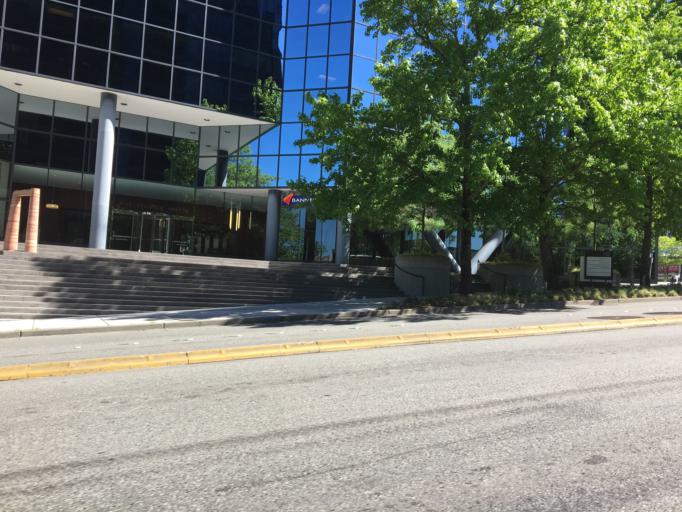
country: US
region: Washington
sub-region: King County
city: Bellevue
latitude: 47.6138
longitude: -122.1973
